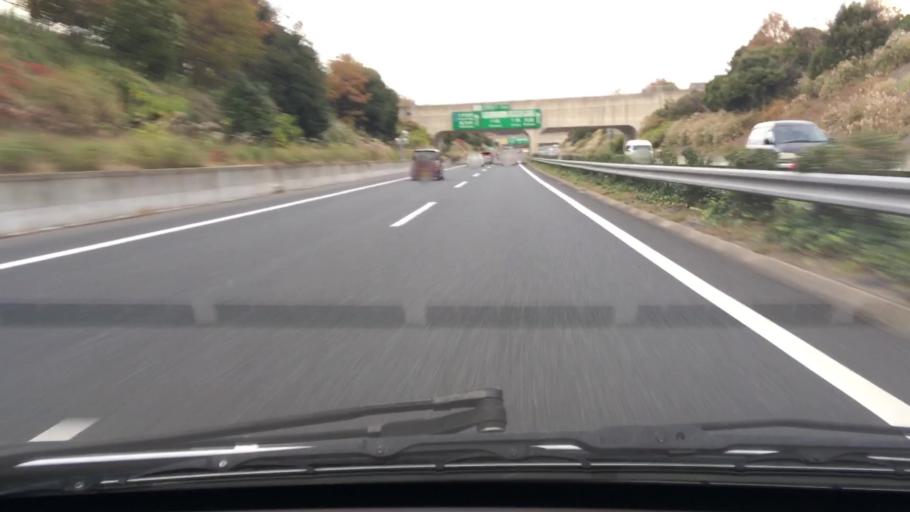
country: JP
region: Chiba
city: Kisarazu
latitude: 35.3421
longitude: 139.9444
